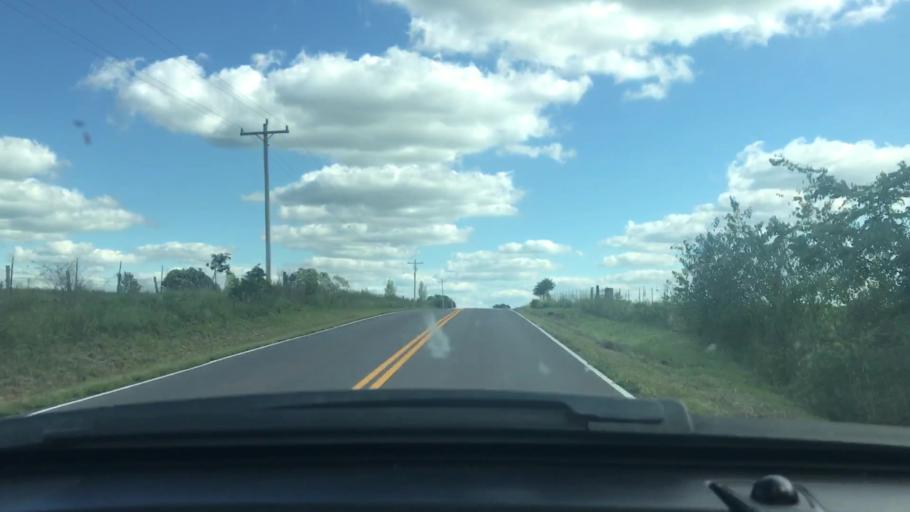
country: US
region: Missouri
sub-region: Wright County
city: Mountain Grove
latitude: 37.3097
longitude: -92.3160
